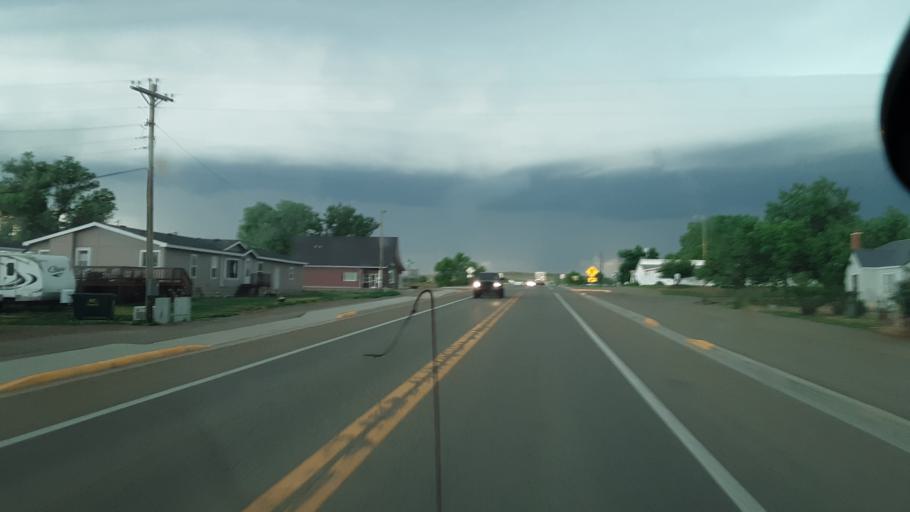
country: US
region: Montana
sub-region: Powder River County
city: Broadus
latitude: 45.4435
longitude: -105.4102
